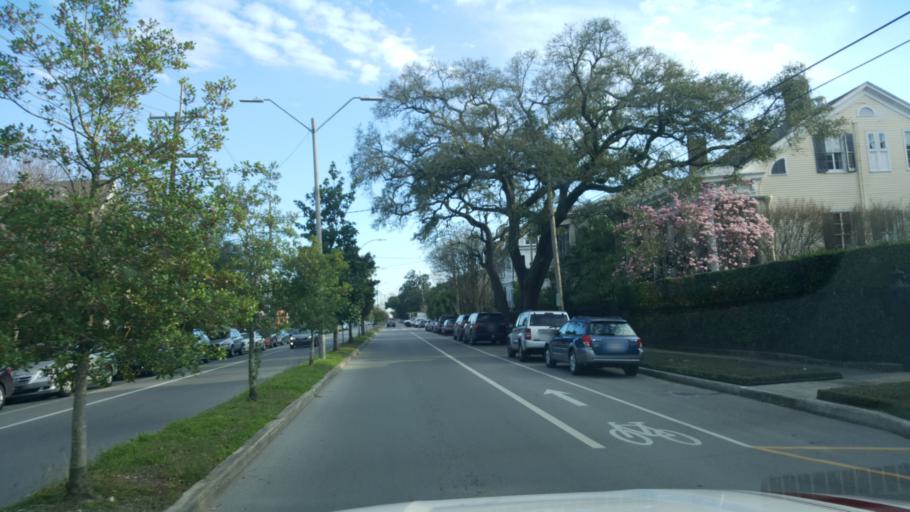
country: US
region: Louisiana
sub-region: Orleans Parish
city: New Orleans
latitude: 29.9313
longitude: -90.0782
